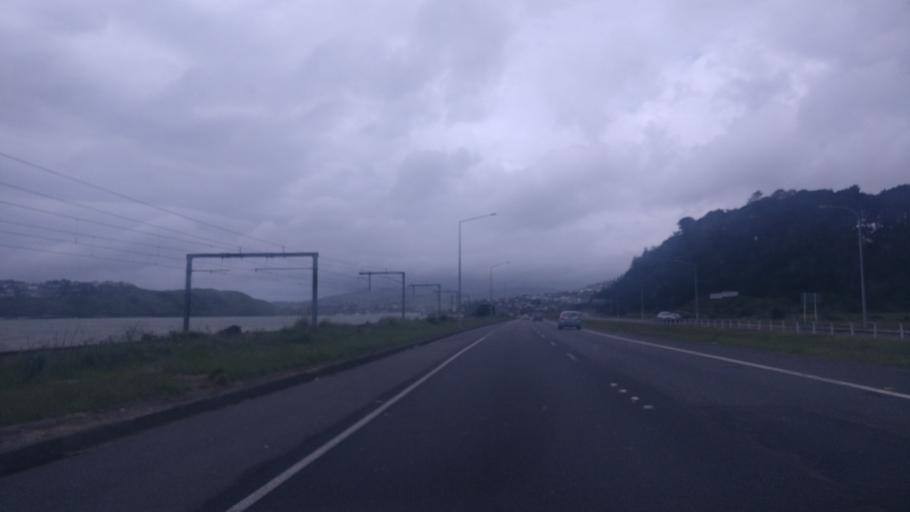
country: NZ
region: Wellington
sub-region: Porirua City
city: Porirua
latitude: -41.1256
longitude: 174.8479
